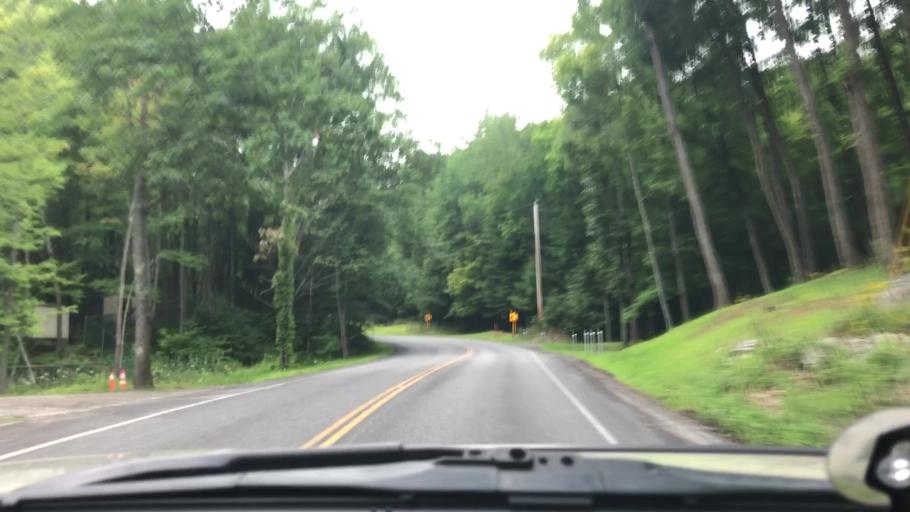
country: US
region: New York
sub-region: Saratoga County
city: Corinth
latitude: 43.1941
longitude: -73.7561
